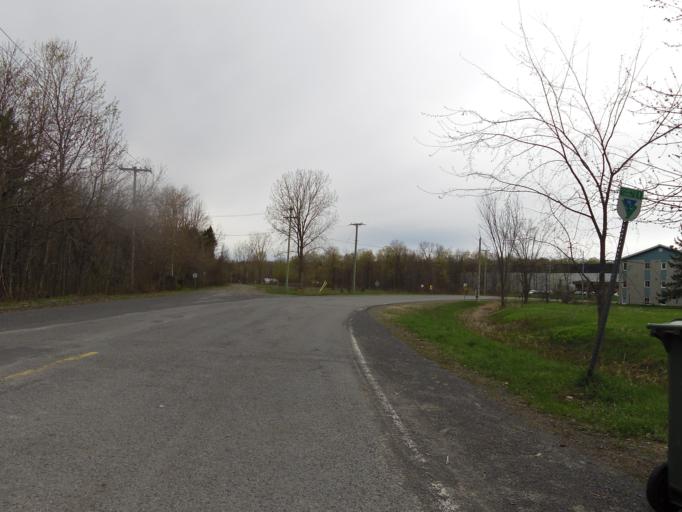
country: CA
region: Quebec
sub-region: Monteregie
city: Hudson
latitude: 45.5282
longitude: -74.2097
